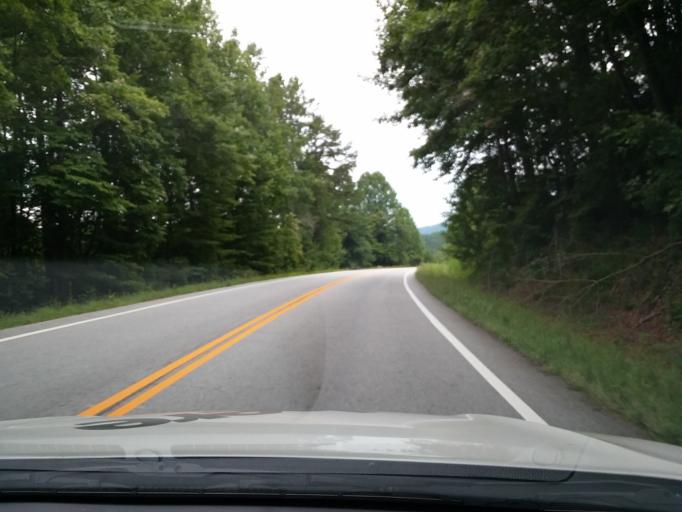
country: US
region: Georgia
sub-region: Rabun County
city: Clayton
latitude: 34.8261
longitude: -83.3221
